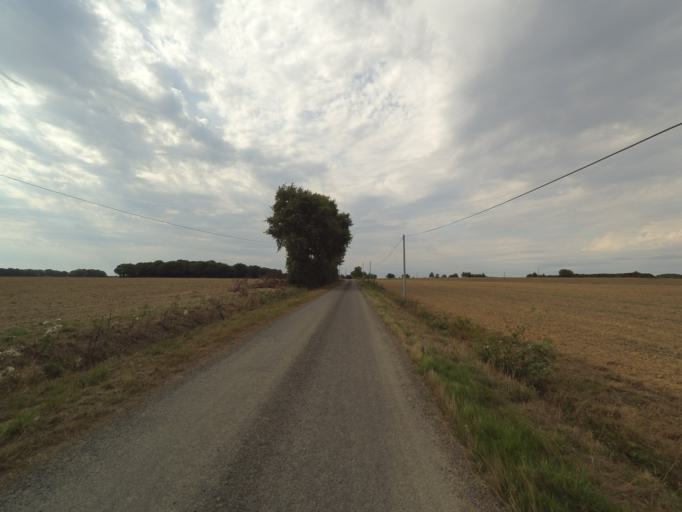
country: FR
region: Pays de la Loire
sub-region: Departement de la Vendee
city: Bouffere
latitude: 46.9708
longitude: -1.3672
